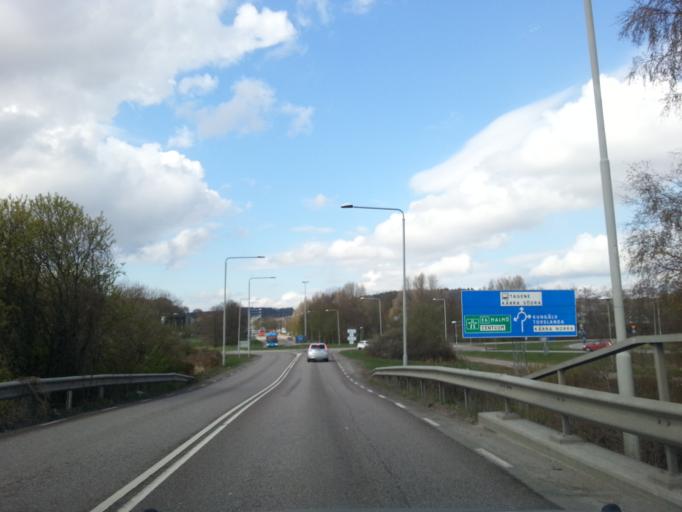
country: SE
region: Vaestra Goetaland
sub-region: Goteborg
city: Gardsten
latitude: 57.7877
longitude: 12.0005
